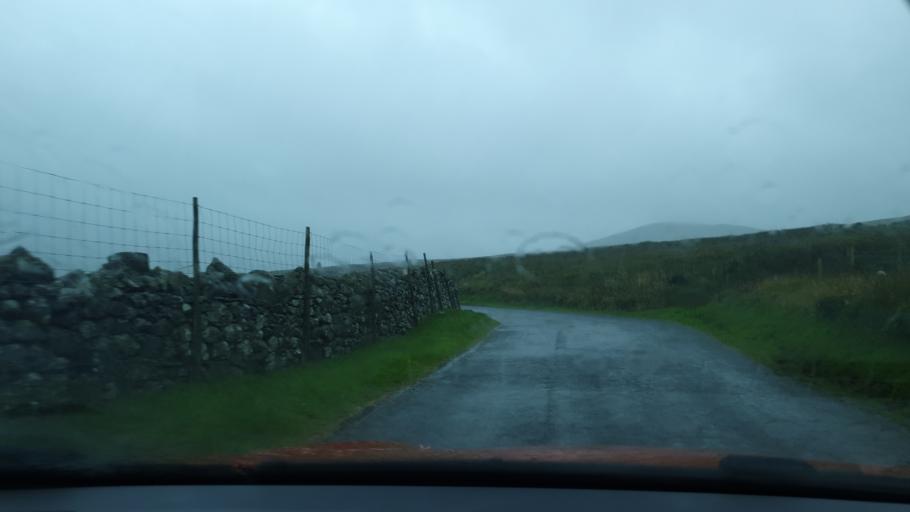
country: GB
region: England
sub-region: Cumbria
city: Millom
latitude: 54.3435
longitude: -3.2490
